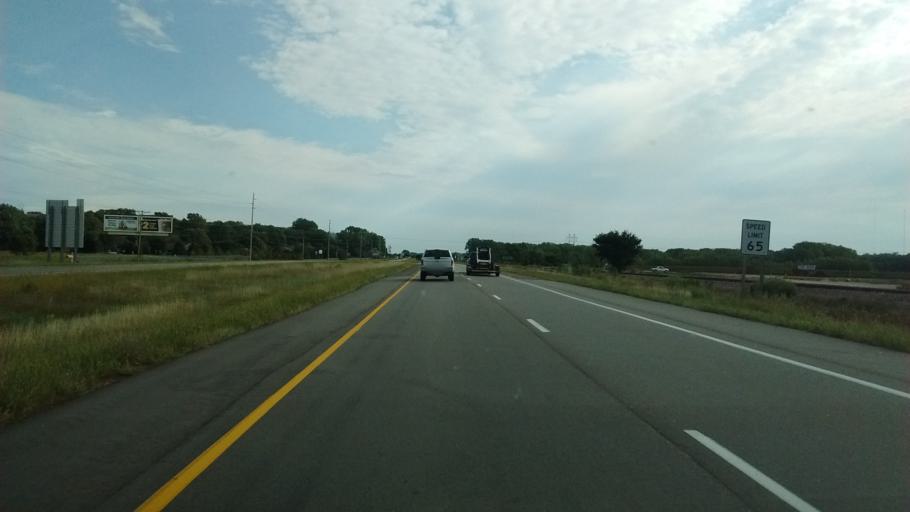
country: US
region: Iowa
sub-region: Woodbury County
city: Sioux City
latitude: 42.5625
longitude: -96.3305
